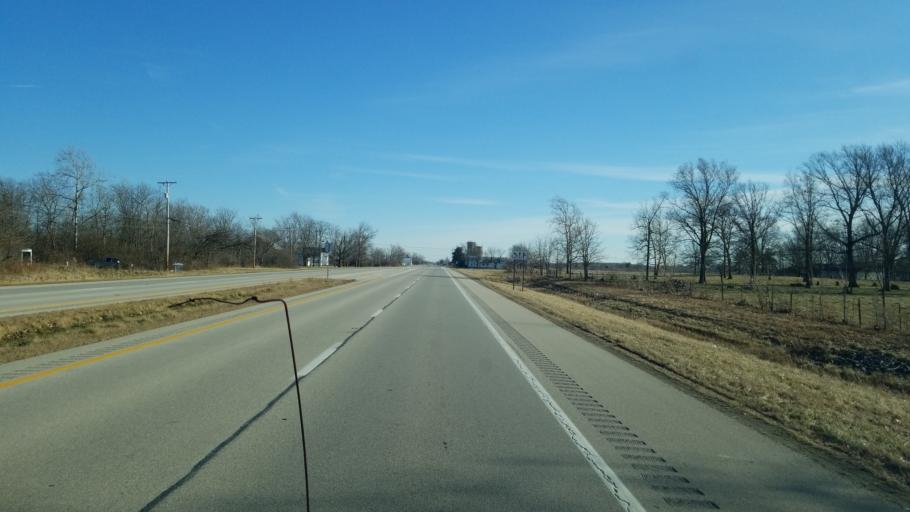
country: US
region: Ohio
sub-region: Sandusky County
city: Gibsonburg
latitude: 41.4295
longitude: -83.3113
